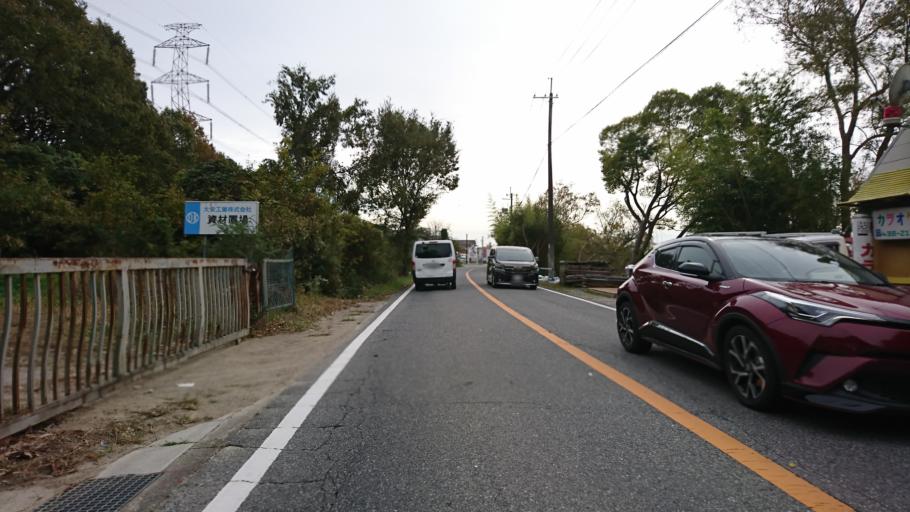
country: JP
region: Hyogo
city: Ono
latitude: 34.8016
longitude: 134.9251
